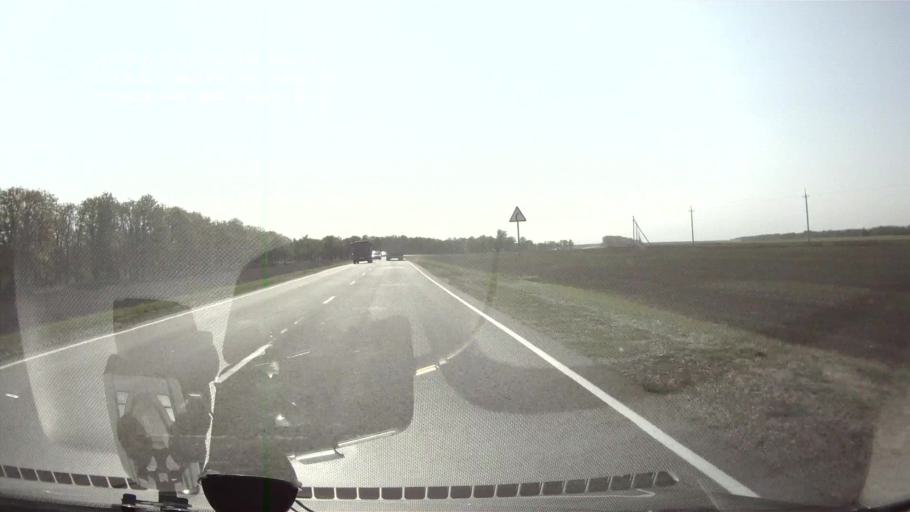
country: RU
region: Krasnodarskiy
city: Novopokrovskaya
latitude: 45.9102
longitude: 40.7201
